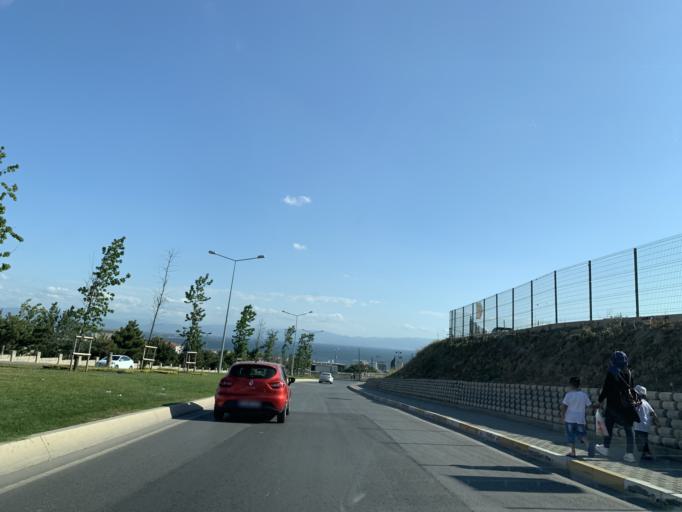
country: TR
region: Istanbul
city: Pendik
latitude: 40.8856
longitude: 29.2600
